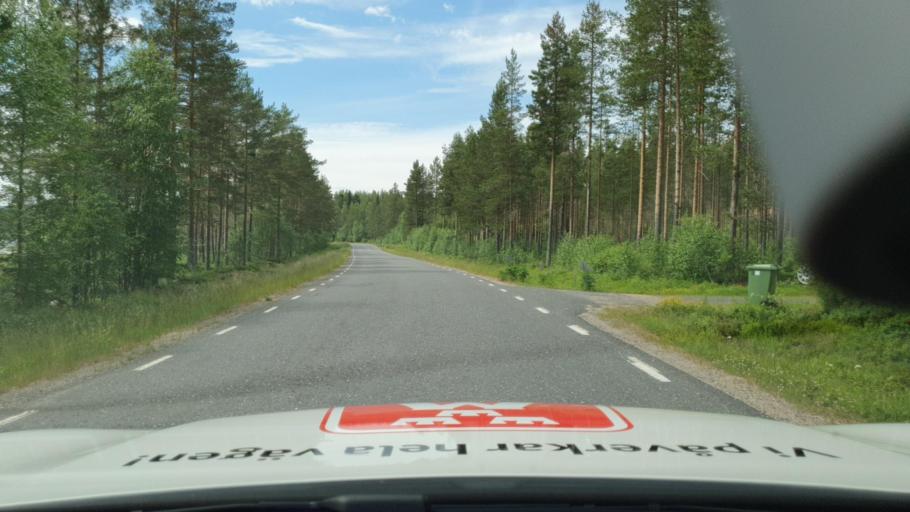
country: SE
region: Vaermland
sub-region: Torsby Kommun
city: Torsby
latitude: 60.6761
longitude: 12.6840
